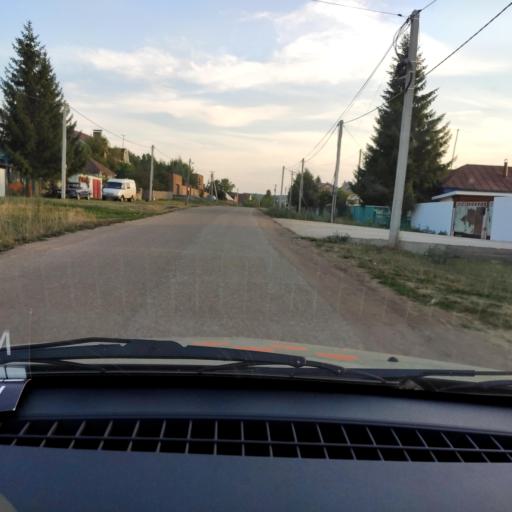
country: RU
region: Bashkortostan
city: Avdon
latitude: 54.5893
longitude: 55.6755
